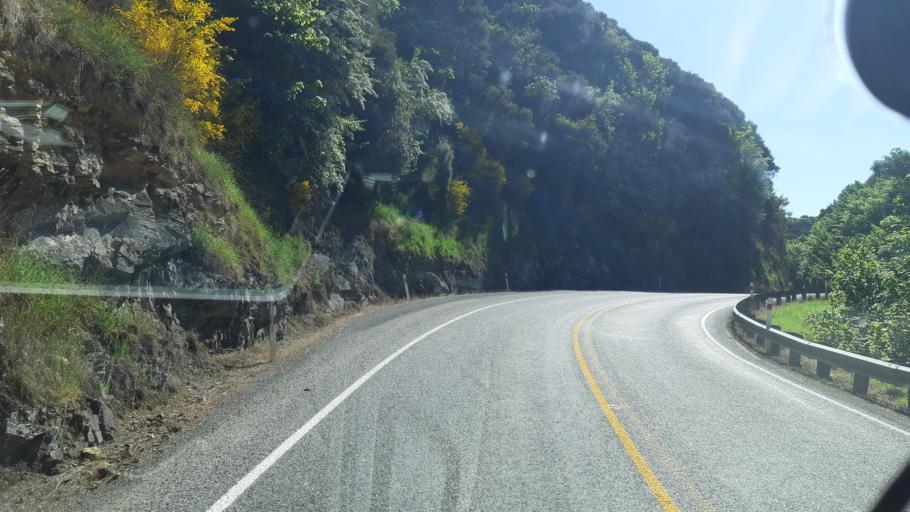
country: NZ
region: Otago
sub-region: Clutha District
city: Milton
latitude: -46.0728
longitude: 169.8392
